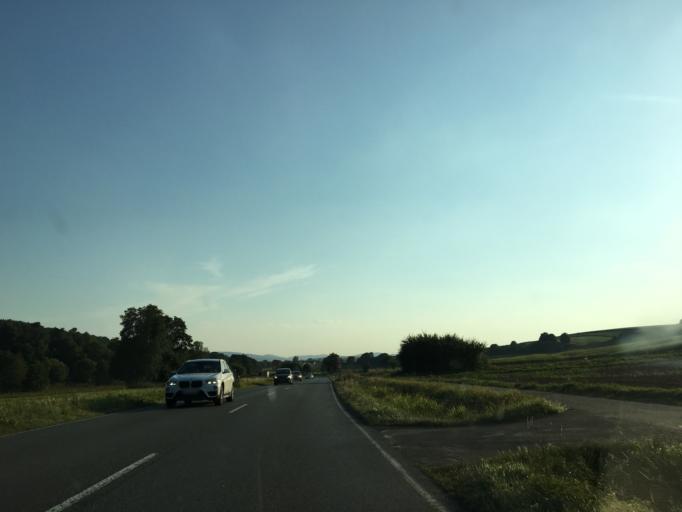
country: DE
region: Hesse
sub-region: Regierungsbezirk Giessen
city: Munchhausen
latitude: 50.9745
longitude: 8.7267
